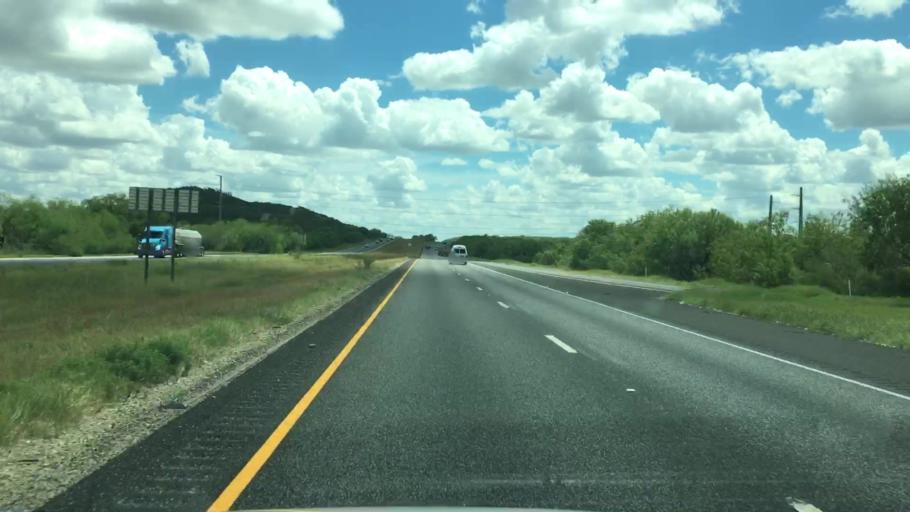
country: US
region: Texas
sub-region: Live Oak County
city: Three Rivers
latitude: 28.7285
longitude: -98.2876
